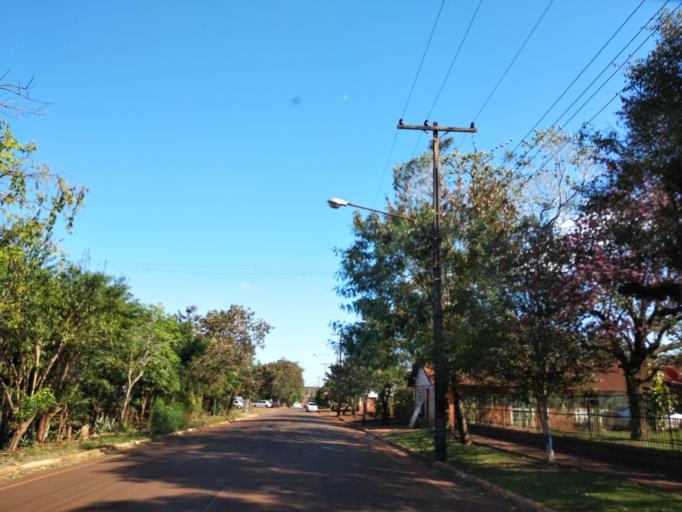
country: PY
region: Itapua
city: Hohenau
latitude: -27.0556
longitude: -55.7445
